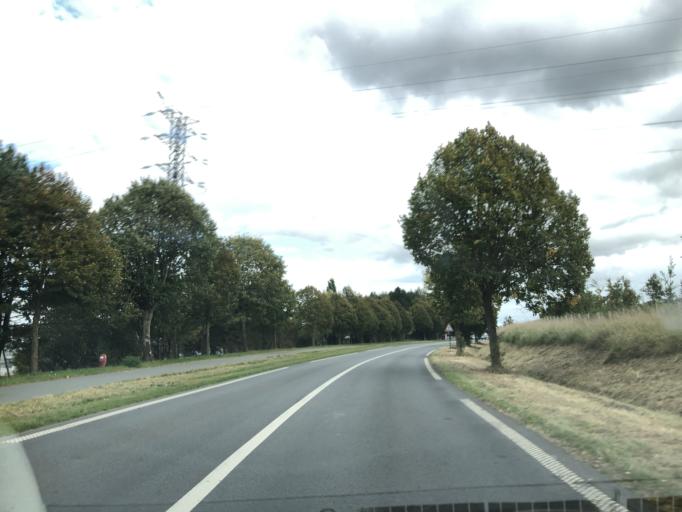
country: FR
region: Nord-Pas-de-Calais
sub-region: Departement du Pas-de-Calais
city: Hesdin
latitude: 50.3657
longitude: 2.0360
